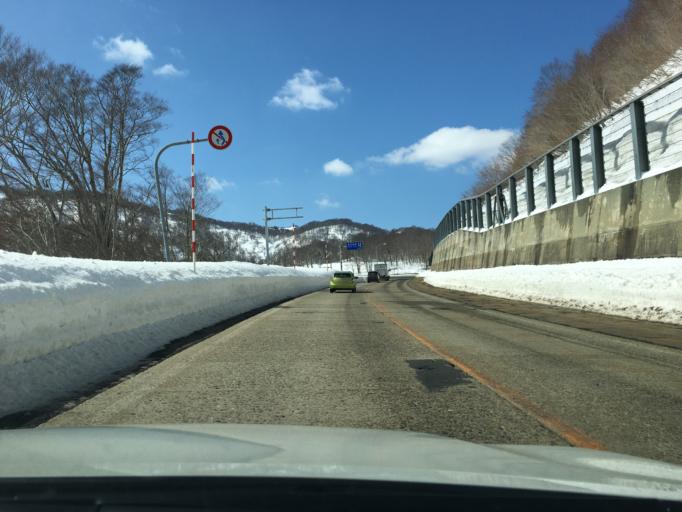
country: JP
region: Yamagata
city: Tsuruoka
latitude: 38.4933
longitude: 139.9782
